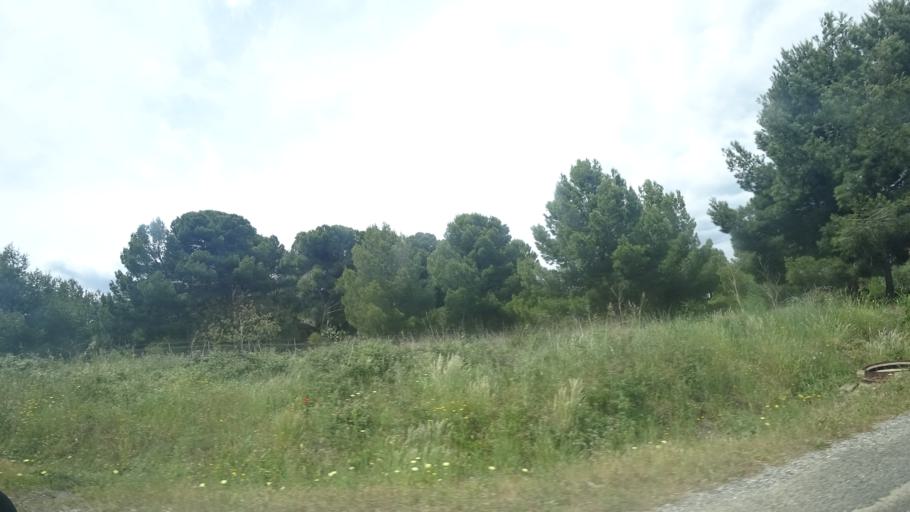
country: FR
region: Languedoc-Roussillon
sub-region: Departement de l'Aude
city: Leucate
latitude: 42.9045
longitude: 3.0359
